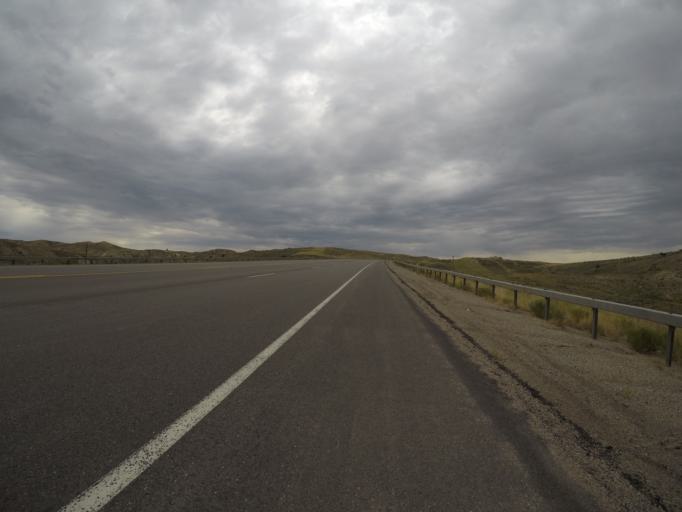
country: US
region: Wyoming
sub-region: Lincoln County
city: Kemmerer
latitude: 41.8088
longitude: -110.6125
